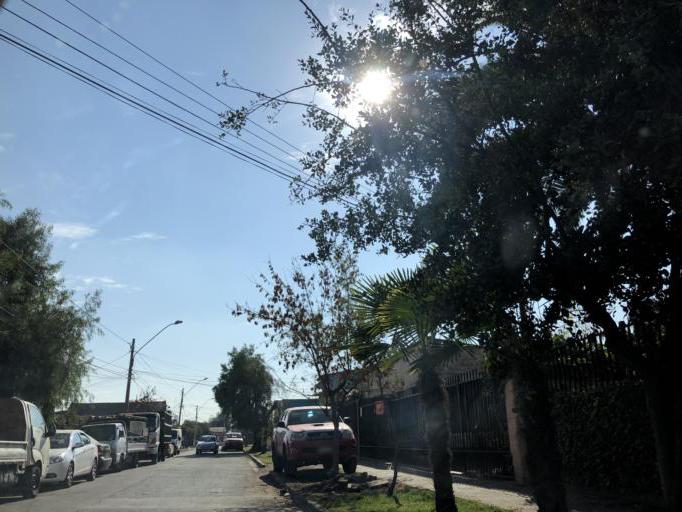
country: CL
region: Santiago Metropolitan
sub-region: Provincia de Cordillera
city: Puente Alto
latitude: -33.6155
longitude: -70.5723
